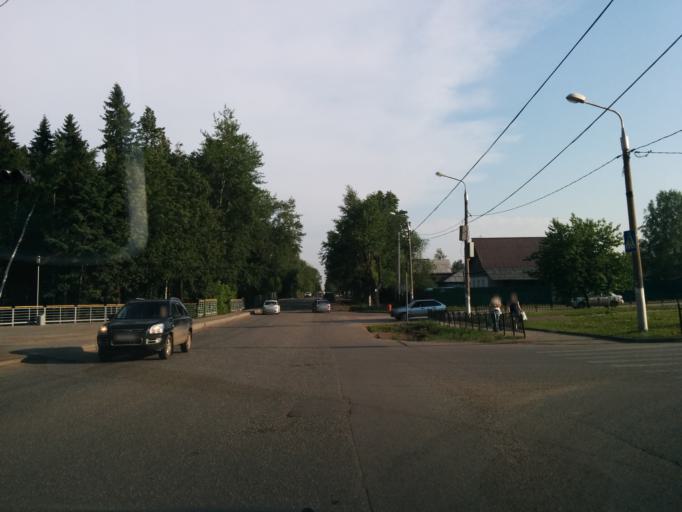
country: RU
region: Perm
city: Perm
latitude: 58.1132
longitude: 56.2968
